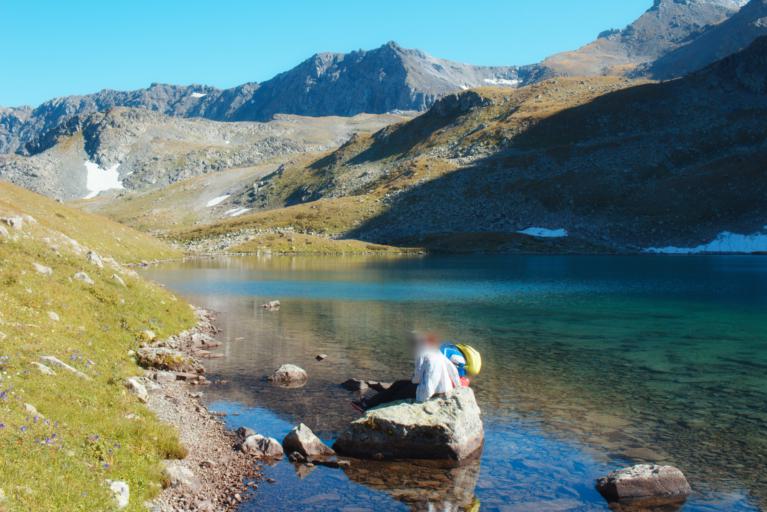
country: RU
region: Karachayevo-Cherkesiya
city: Mednogorskiy
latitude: 43.6100
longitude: 41.1364
